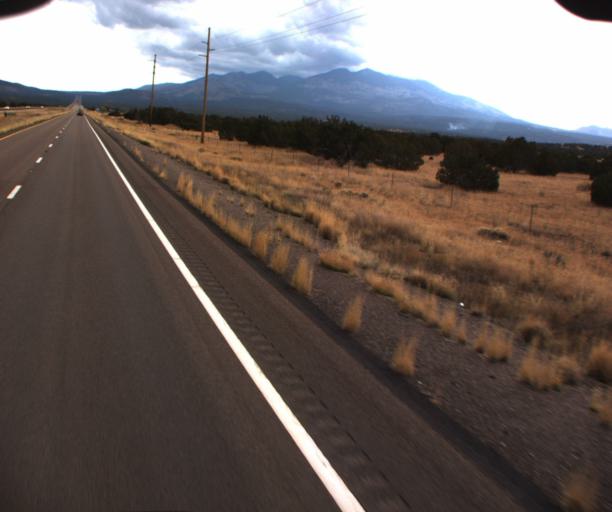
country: US
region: Arizona
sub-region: Coconino County
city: Flagstaff
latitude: 35.4616
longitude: -111.5605
